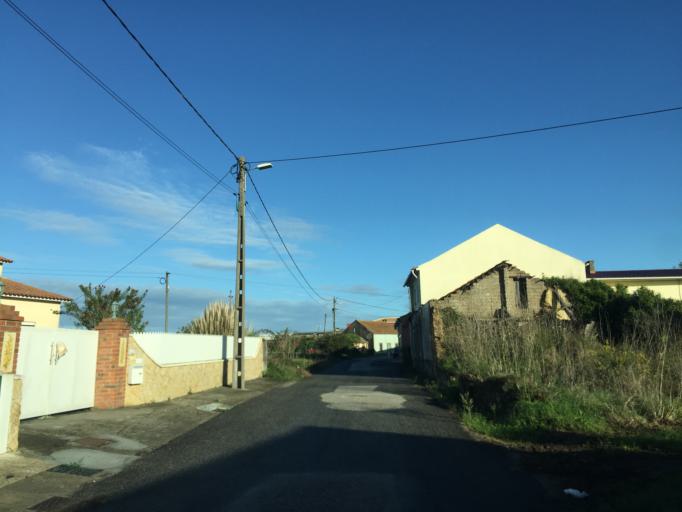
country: PT
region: Coimbra
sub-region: Figueira da Foz
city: Lavos
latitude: 40.0564
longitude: -8.8090
